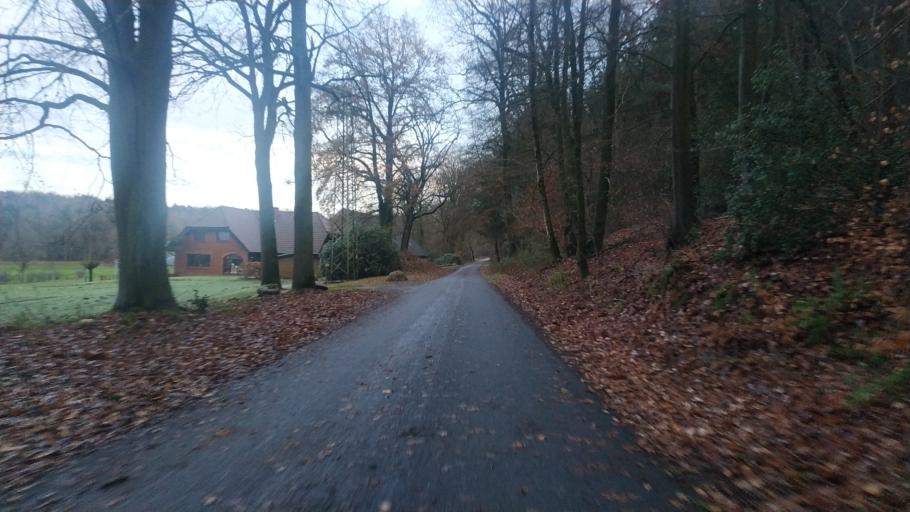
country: DE
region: North Rhine-Westphalia
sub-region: Regierungsbezirk Munster
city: Horstel
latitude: 52.2782
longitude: 7.6105
